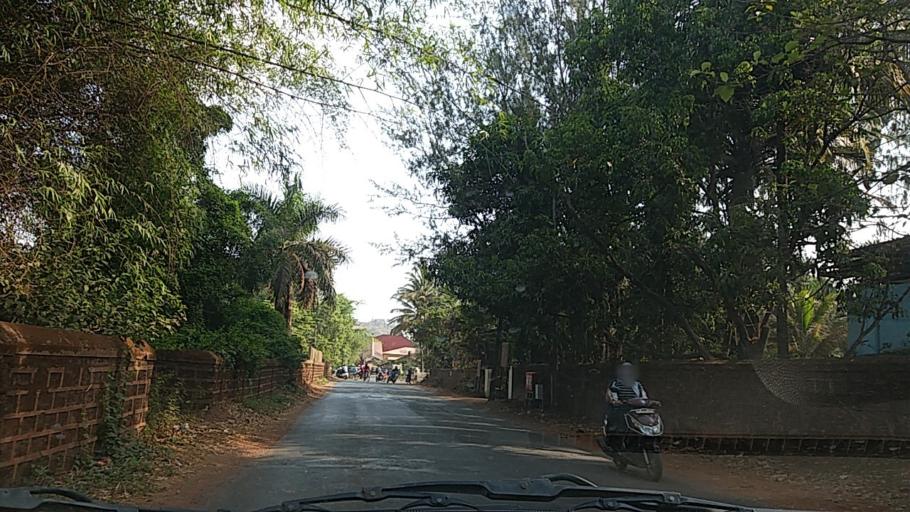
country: IN
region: Goa
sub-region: South Goa
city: Madgaon
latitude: 15.2656
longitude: 73.9701
